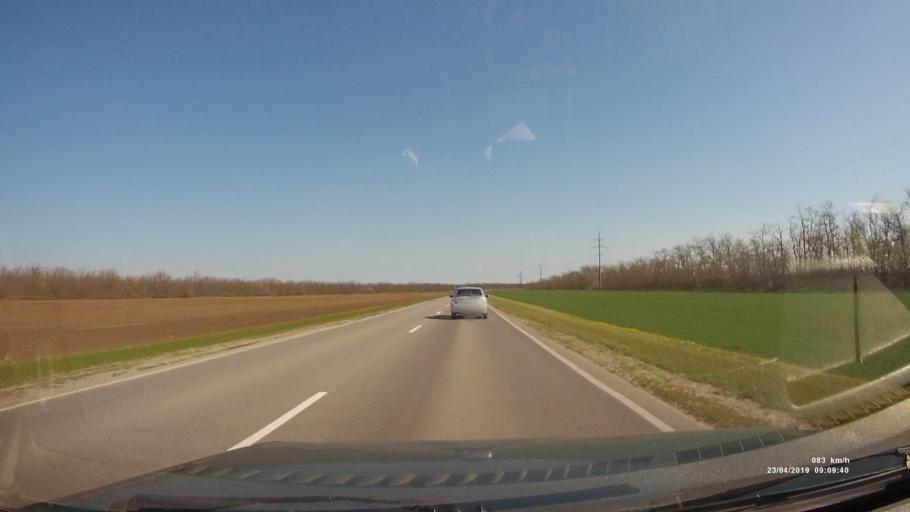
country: RU
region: Rostov
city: Sal'sk
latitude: 46.5768
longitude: 41.6144
